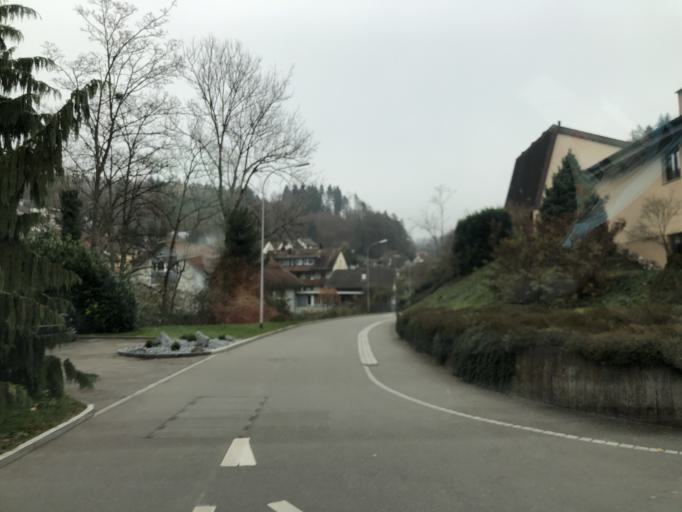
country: CH
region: Aargau
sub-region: Bezirk Baden
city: Gebenstorf
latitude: 47.4785
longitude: 8.2458
